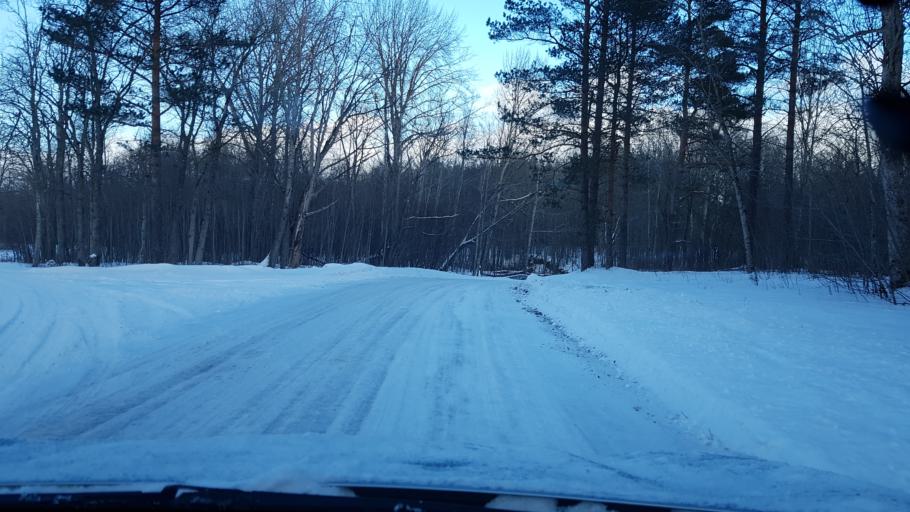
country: EE
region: Harju
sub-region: Nissi vald
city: Turba
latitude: 59.2212
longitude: 24.1414
